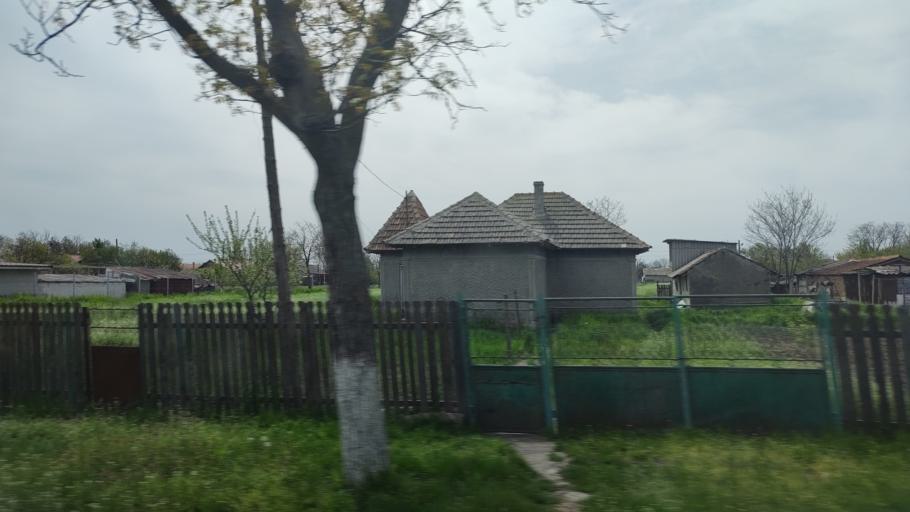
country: RO
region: Constanta
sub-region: Comuna Cobadin
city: Viisoara
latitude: 44.0772
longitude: 28.1869
